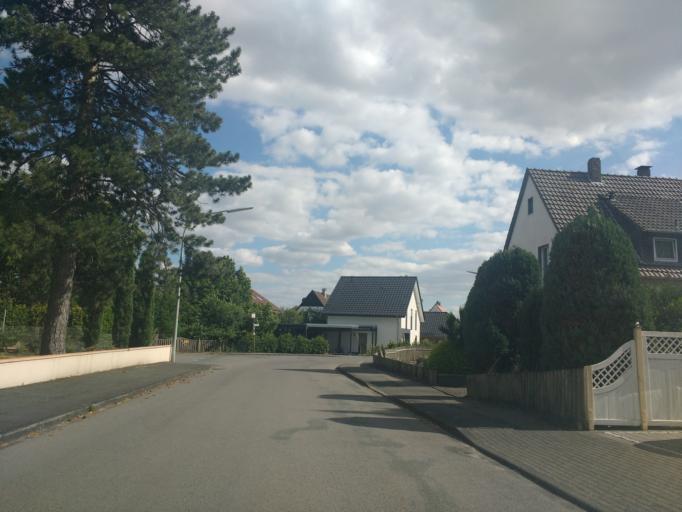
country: DE
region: North Rhine-Westphalia
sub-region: Regierungsbezirk Detmold
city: Schlangen
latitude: 51.8015
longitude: 8.8343
